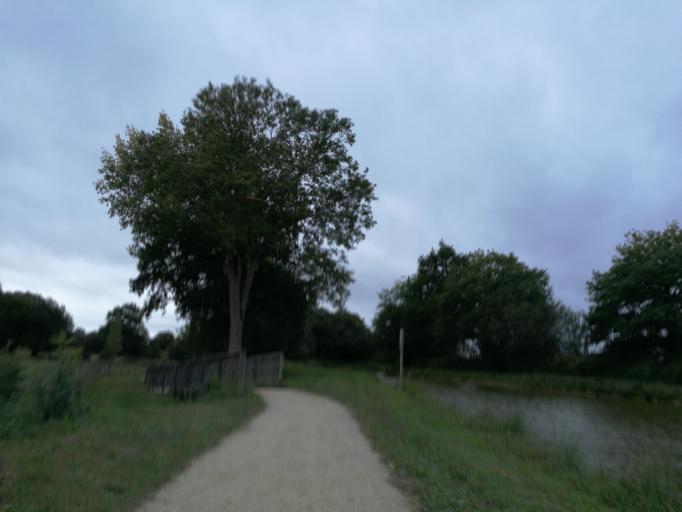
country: FR
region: Brittany
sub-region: Departement d'Ille-et-Vilaine
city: Bedee
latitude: 48.1742
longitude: -1.9477
